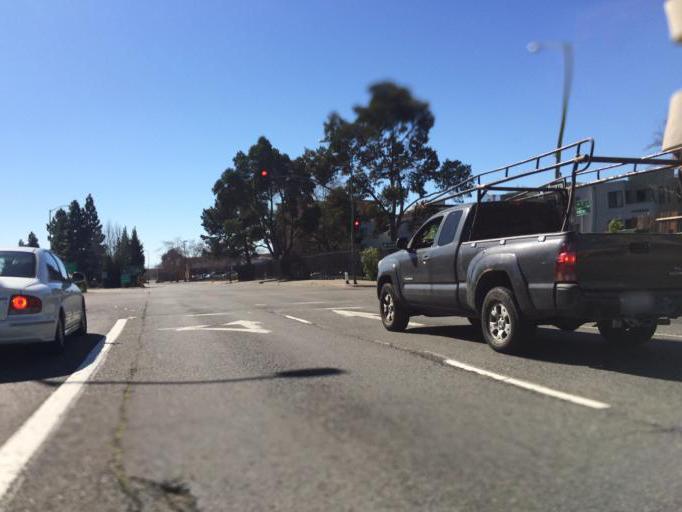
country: US
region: California
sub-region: Alameda County
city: Oakland
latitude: 37.8055
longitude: -122.2797
